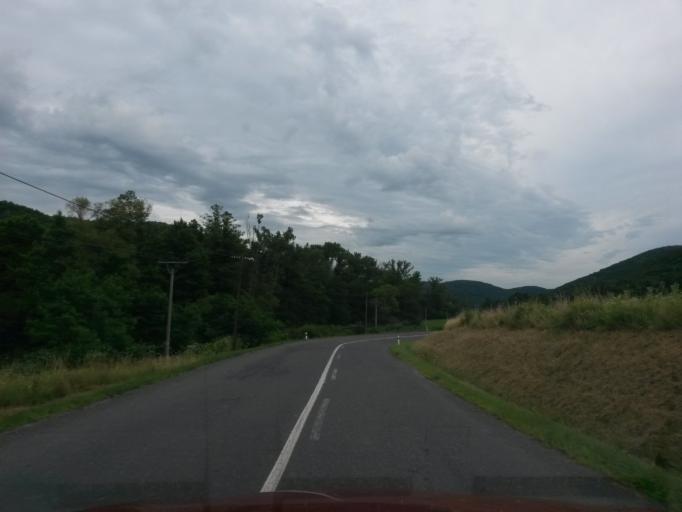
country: SK
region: Banskobystricky
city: Velky Krtis
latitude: 48.3476
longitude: 19.4081
